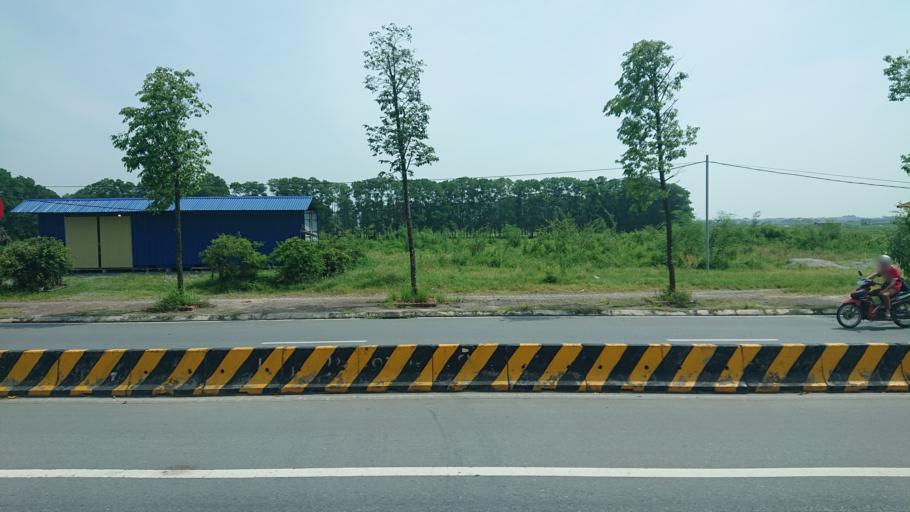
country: VN
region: Ha Noi
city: Soc Son
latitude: 21.2072
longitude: 105.8235
